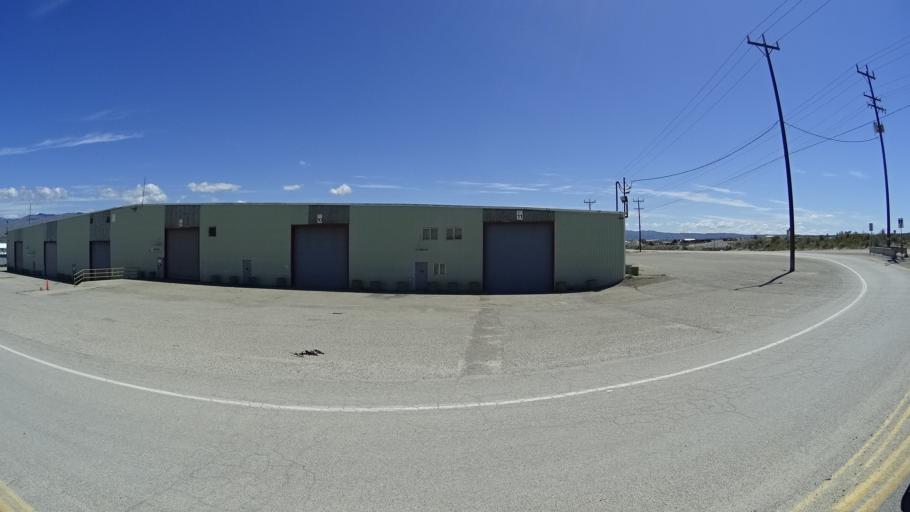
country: US
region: Idaho
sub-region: Ada County
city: Boise
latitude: 43.5609
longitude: -116.1834
